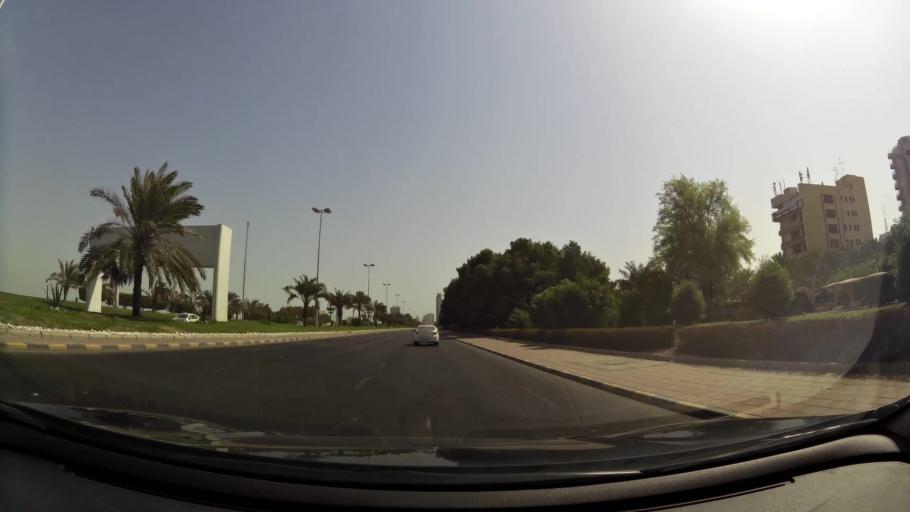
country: KW
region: Muhafazat Hawalli
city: Hawalli
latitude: 29.3502
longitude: 48.0333
